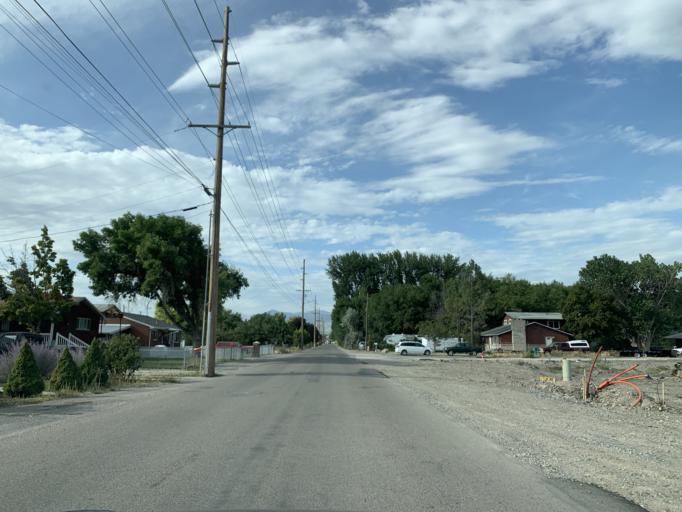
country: US
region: Utah
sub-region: Utah County
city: Provo
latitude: 40.2214
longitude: -111.6873
